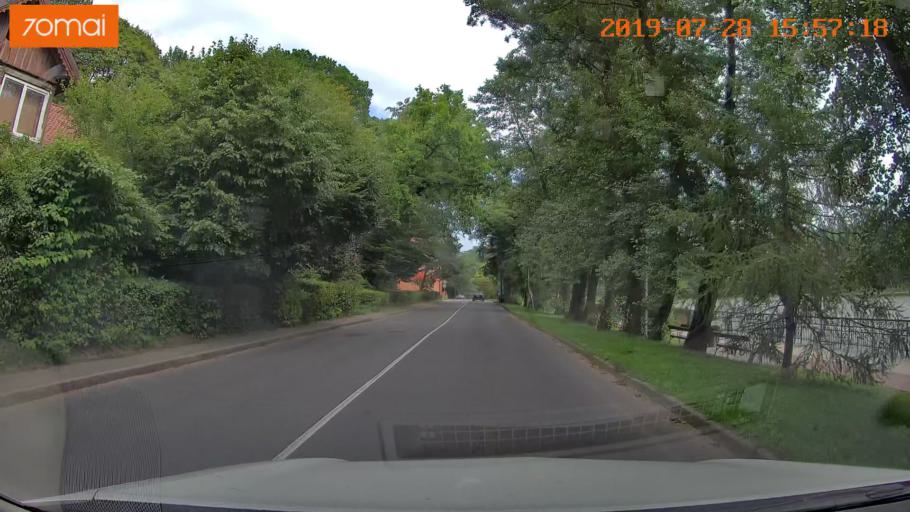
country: RU
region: Kaliningrad
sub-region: Gorod Svetlogorsk
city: Svetlogorsk
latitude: 54.9383
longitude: 20.1536
